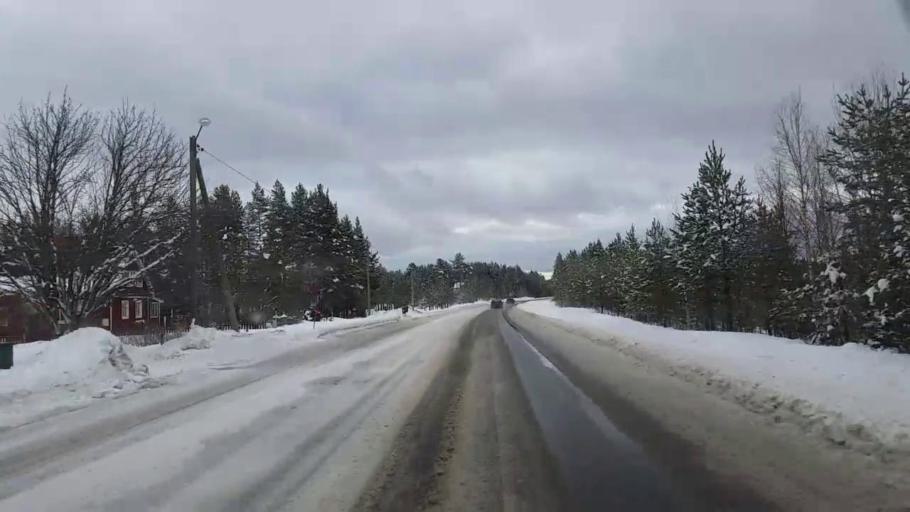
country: SE
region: Vaesternorrland
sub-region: Ange Kommun
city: Ange
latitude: 62.0430
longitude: 15.1824
